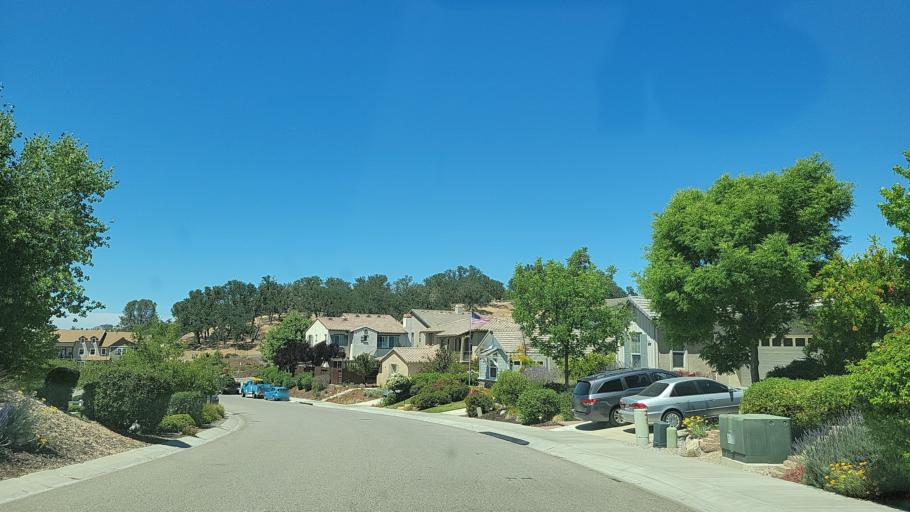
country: US
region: California
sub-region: San Luis Obispo County
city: Atascadero
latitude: 35.4548
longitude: -120.6282
